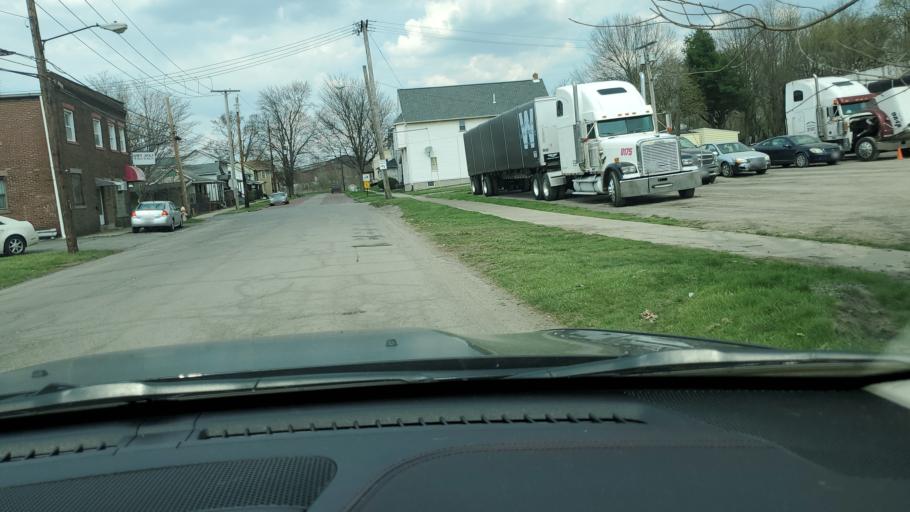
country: US
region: Ohio
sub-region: Trumbull County
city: Niles
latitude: 41.1778
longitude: -80.7570
